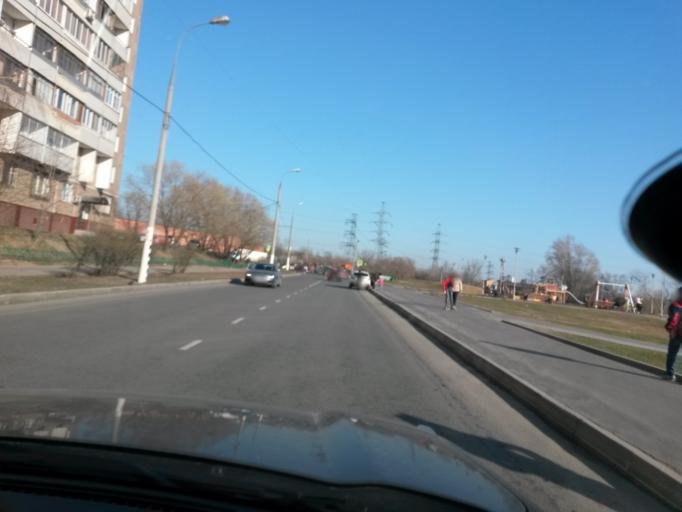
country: RU
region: Moscow
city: Annino
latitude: 55.5722
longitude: 37.5911
